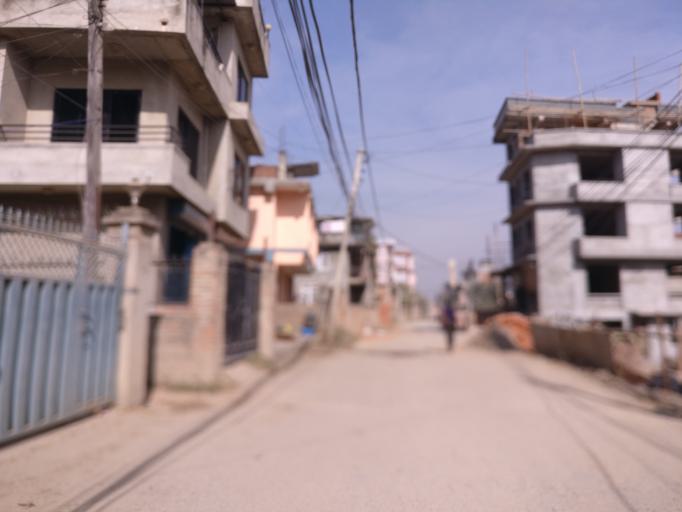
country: NP
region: Central Region
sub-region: Bagmati Zone
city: Patan
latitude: 27.6758
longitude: 85.3300
